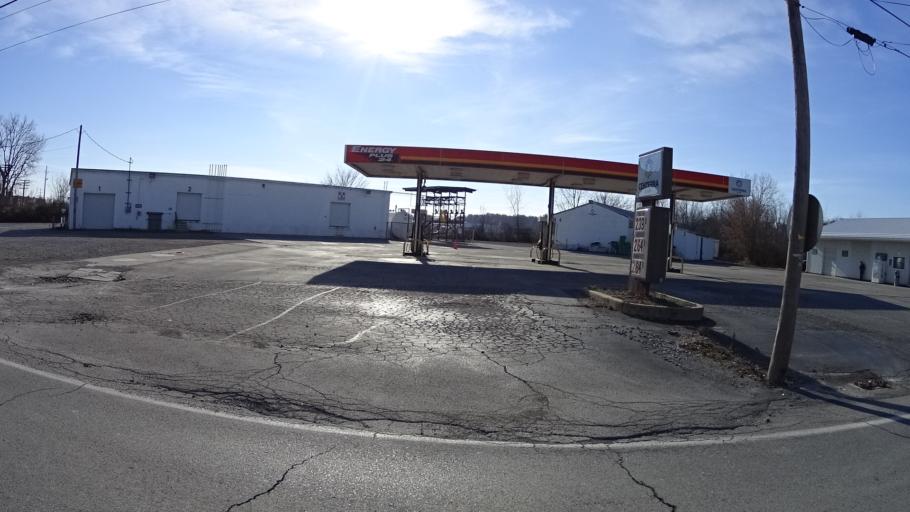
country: US
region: Ohio
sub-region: Lorain County
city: Elyria
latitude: 41.3725
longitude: -82.1224
